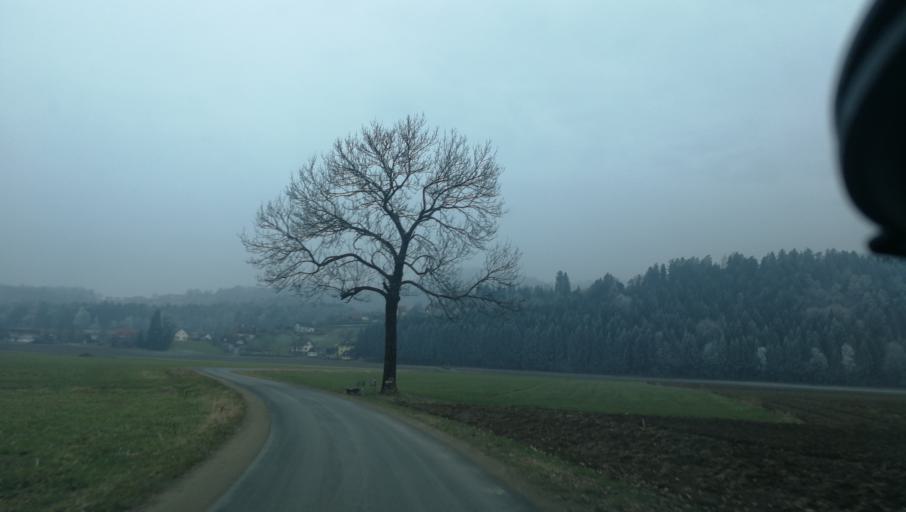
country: AT
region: Styria
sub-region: Politischer Bezirk Deutschlandsberg
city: Stainz
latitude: 46.9007
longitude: 15.2439
